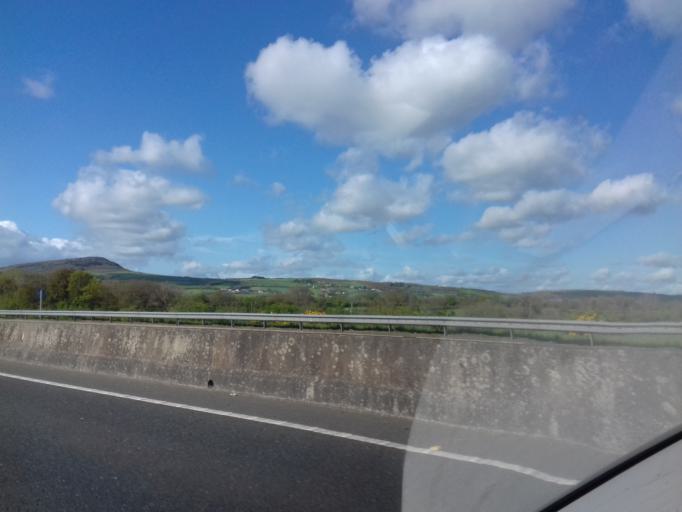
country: IE
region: Munster
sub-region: Waterford
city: Waterford
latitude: 52.3151
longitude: -7.1415
